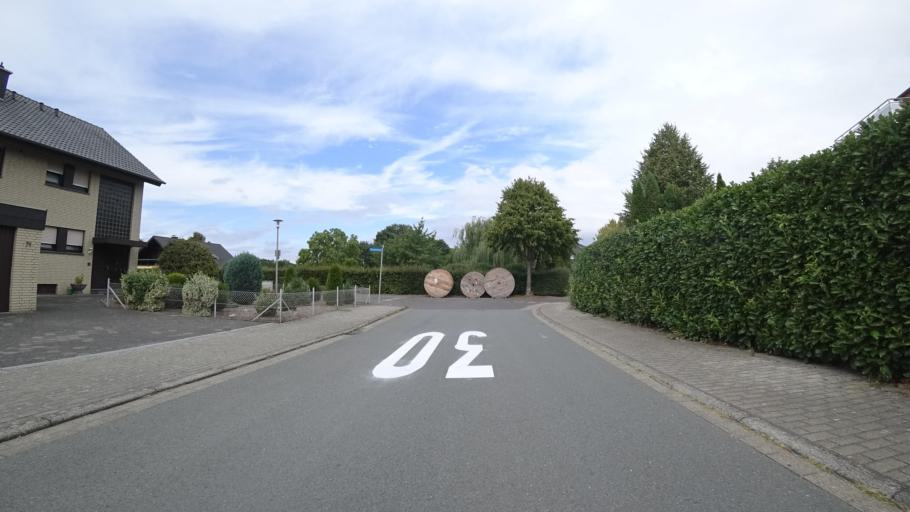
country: DE
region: North Rhine-Westphalia
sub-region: Regierungsbezirk Detmold
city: Verl
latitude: 51.9408
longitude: 8.4704
